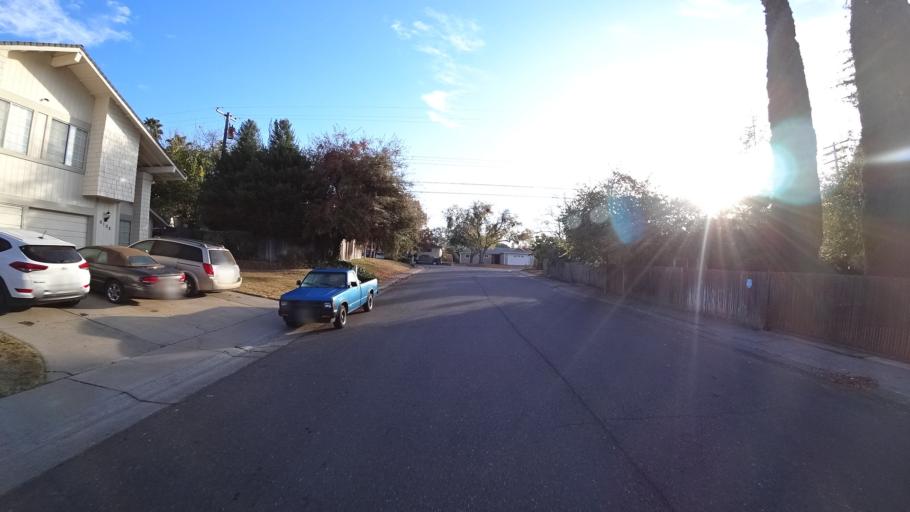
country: US
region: California
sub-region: Sacramento County
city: Citrus Heights
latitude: 38.6763
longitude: -121.3042
